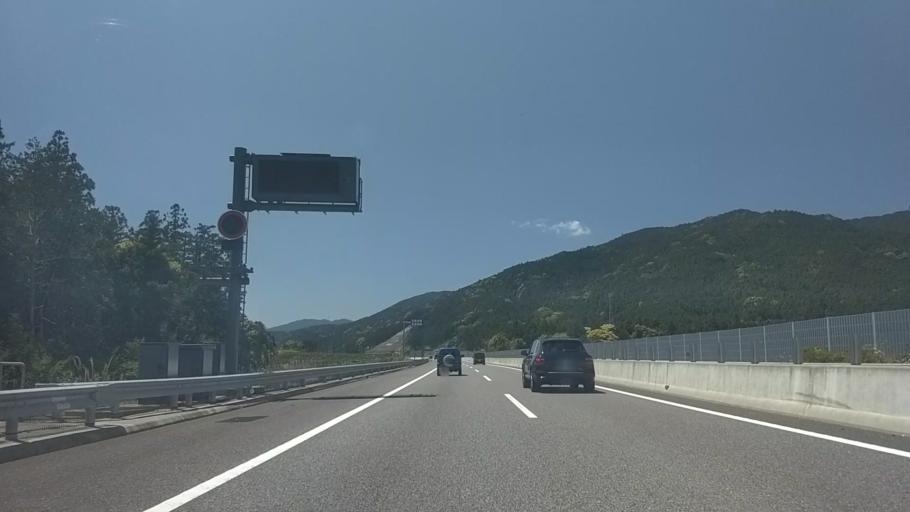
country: JP
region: Aichi
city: Shinshiro
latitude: 34.9272
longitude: 137.5207
